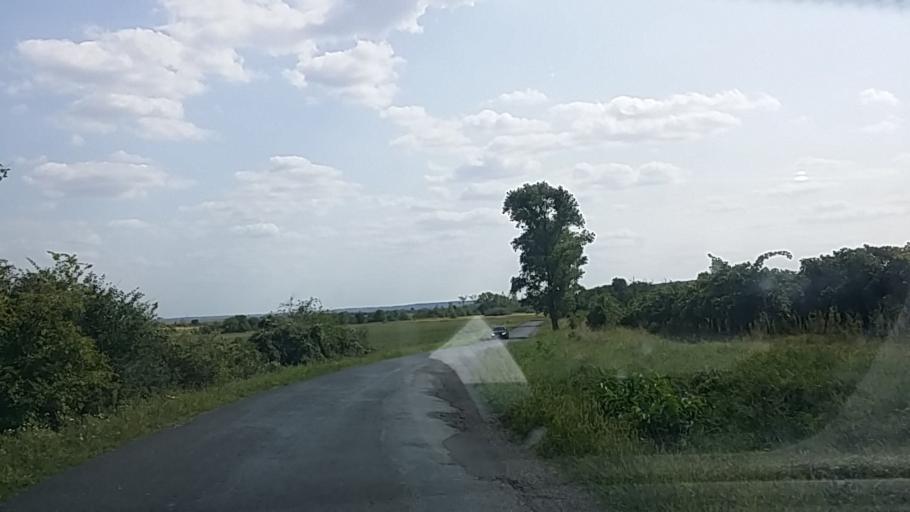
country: HU
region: Gyor-Moson-Sopron
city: Fertorakos
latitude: 47.7032
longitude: 16.6589
